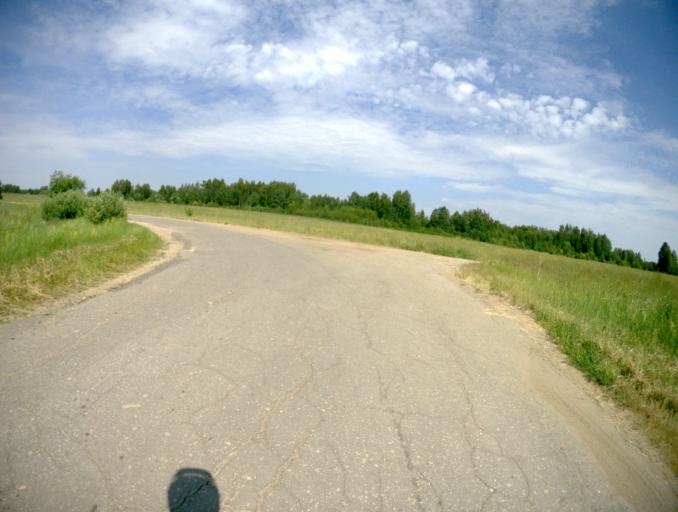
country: RU
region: Vladimir
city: Vorsha
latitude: 56.0243
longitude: 40.1897
